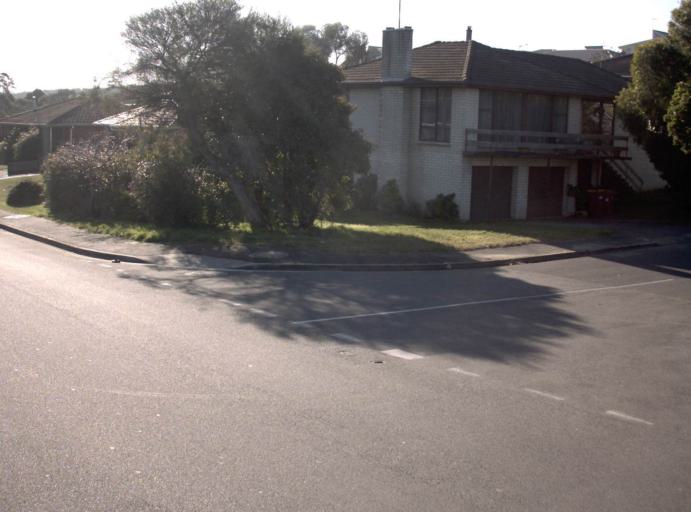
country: AU
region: Tasmania
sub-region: Launceston
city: Summerhill
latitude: -41.4649
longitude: 147.1255
